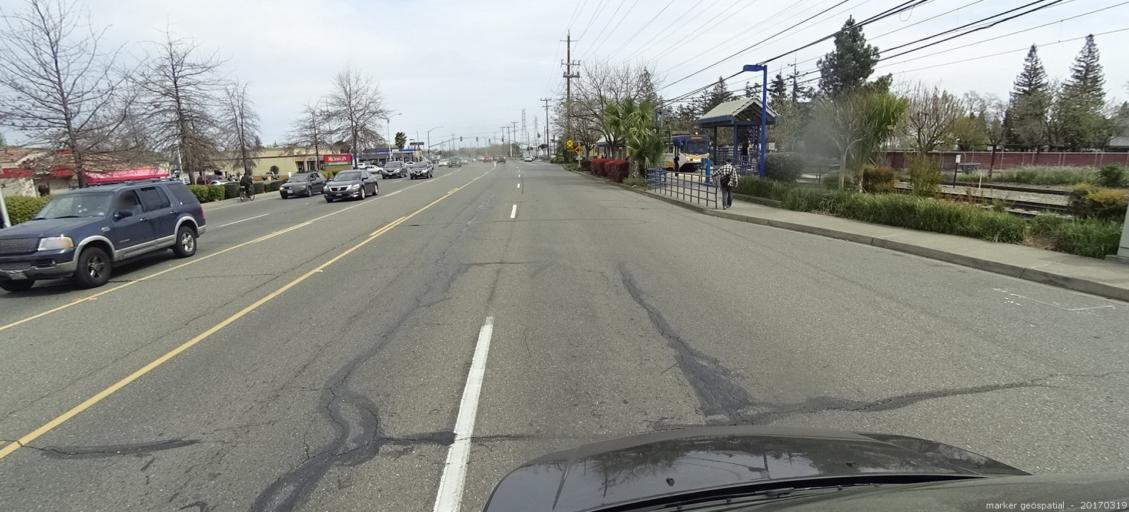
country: US
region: California
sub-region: Sacramento County
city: Rosemont
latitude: 38.5471
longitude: -121.3944
